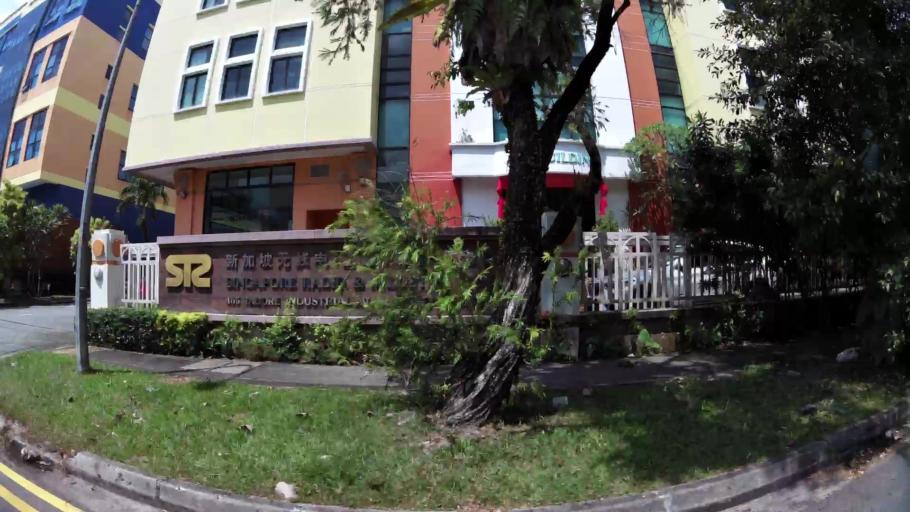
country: MY
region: Johor
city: Kampung Pasir Gudang Baru
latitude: 1.3889
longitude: 103.8291
